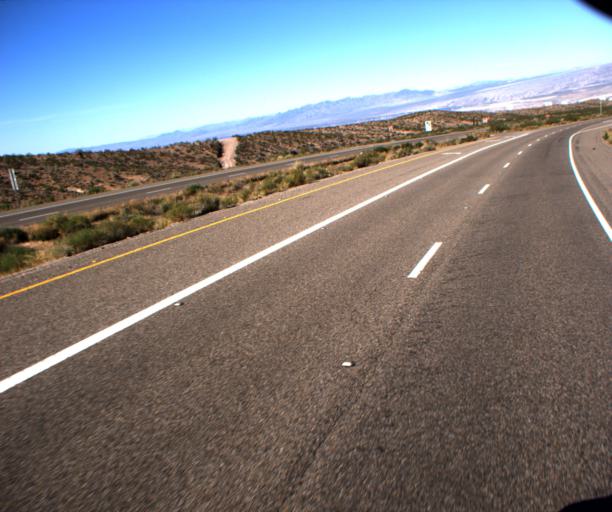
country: US
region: Nevada
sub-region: Clark County
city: Laughlin
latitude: 35.1860
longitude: -114.4540
